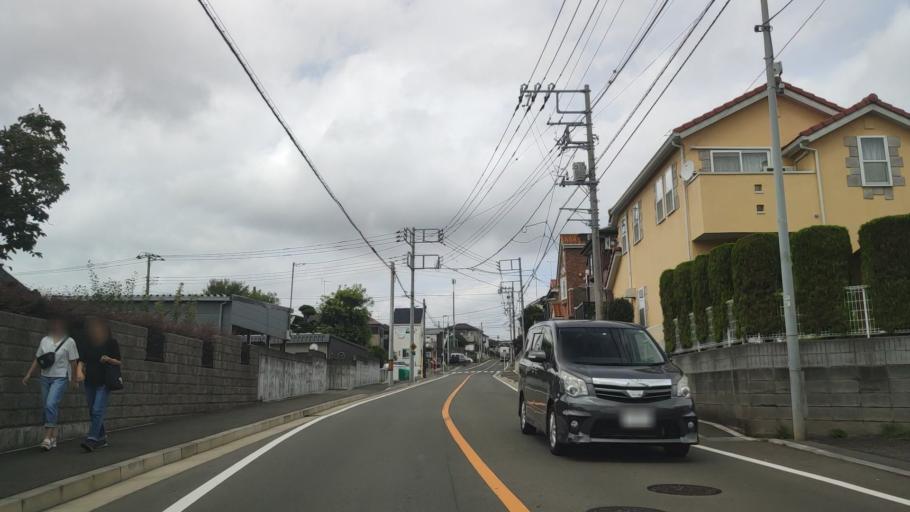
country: JP
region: Kanagawa
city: Minami-rinkan
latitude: 35.4750
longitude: 139.4764
